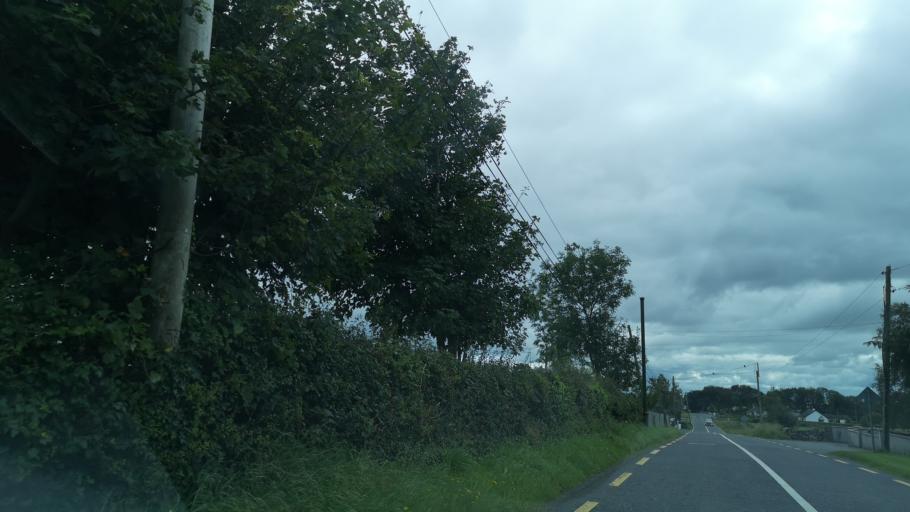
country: IE
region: Connaught
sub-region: County Galway
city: Ballinasloe
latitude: 53.3173
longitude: -8.1715
